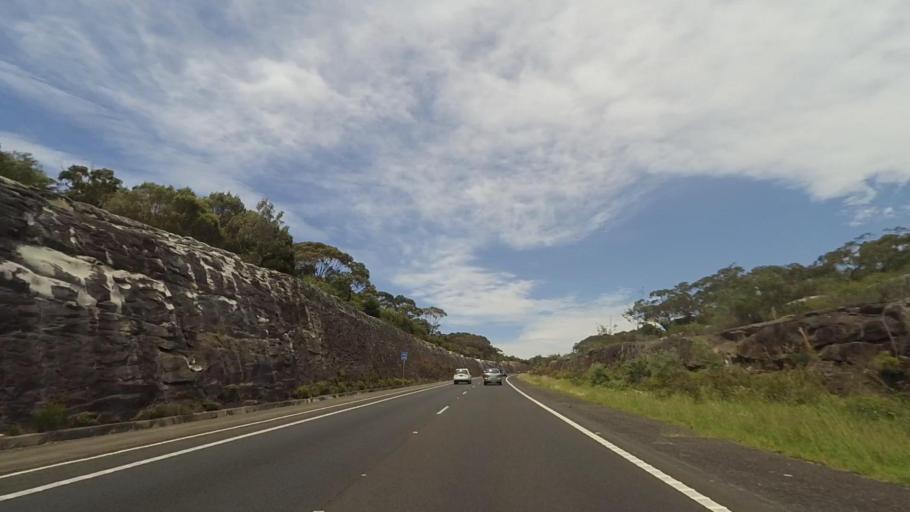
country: AU
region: New South Wales
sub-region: Wollongong
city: Helensburgh
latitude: -34.2394
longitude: 150.9456
